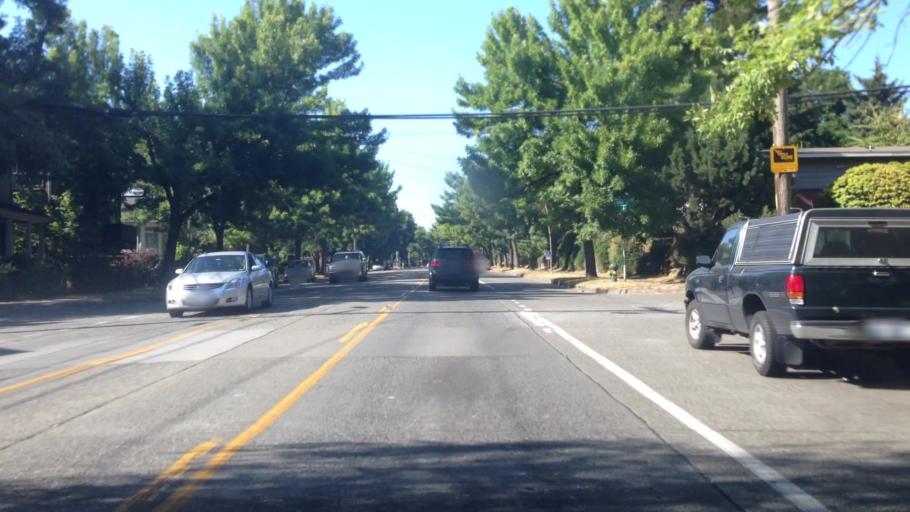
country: US
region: Washington
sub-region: King County
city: Seattle
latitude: 47.5965
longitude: -122.2975
